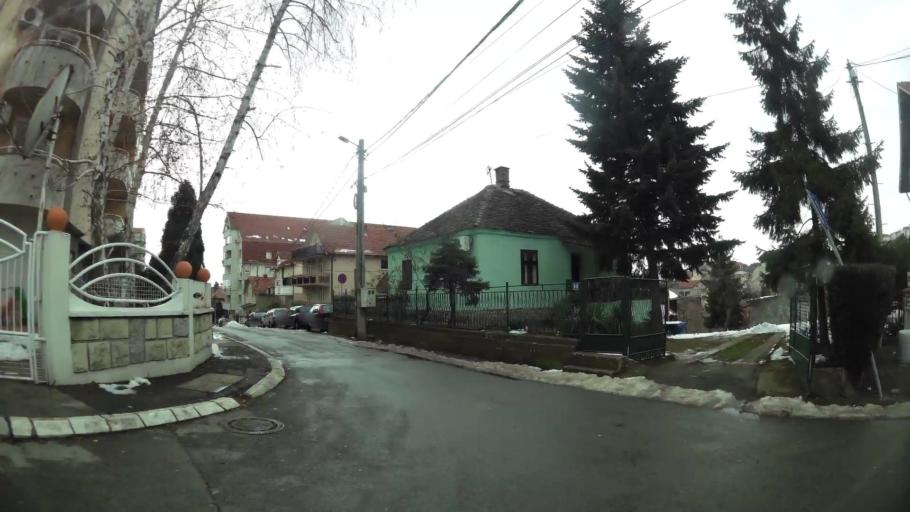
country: RS
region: Central Serbia
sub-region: Belgrade
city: Rakovica
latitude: 44.7555
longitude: 20.4184
